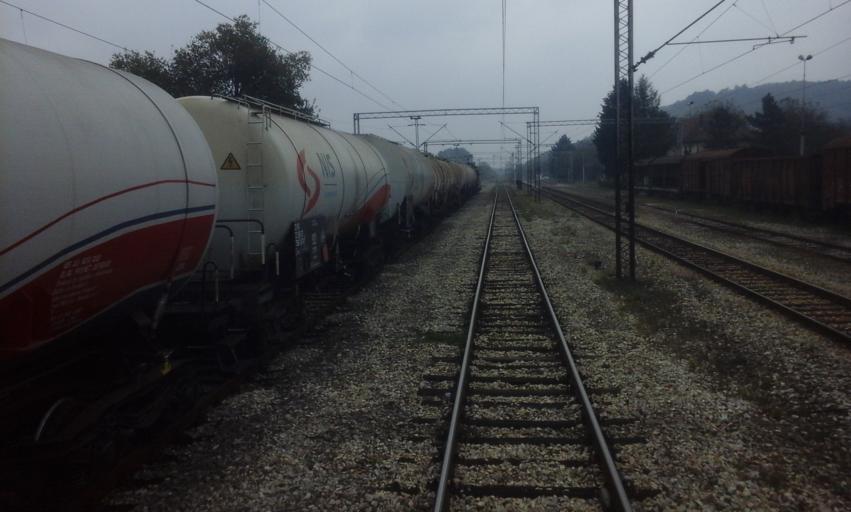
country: RS
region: Central Serbia
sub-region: Sumadijski Okrug
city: Batocina
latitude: 44.0839
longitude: 21.1789
